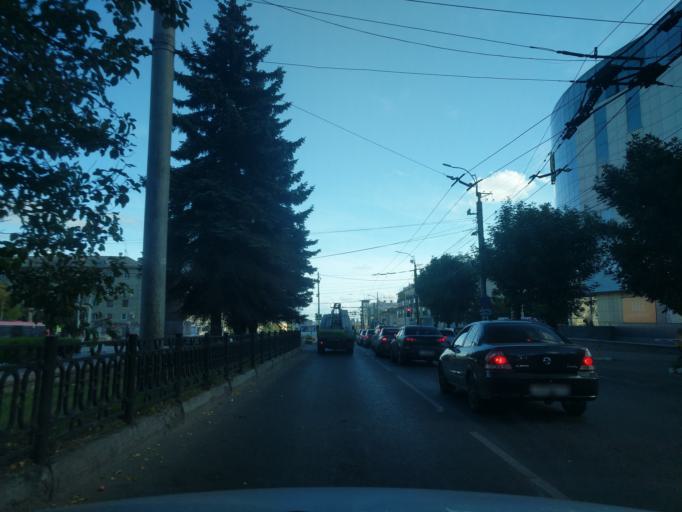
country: RU
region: Kirov
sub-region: Kirovo-Chepetskiy Rayon
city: Kirov
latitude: 58.5946
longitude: 49.6578
